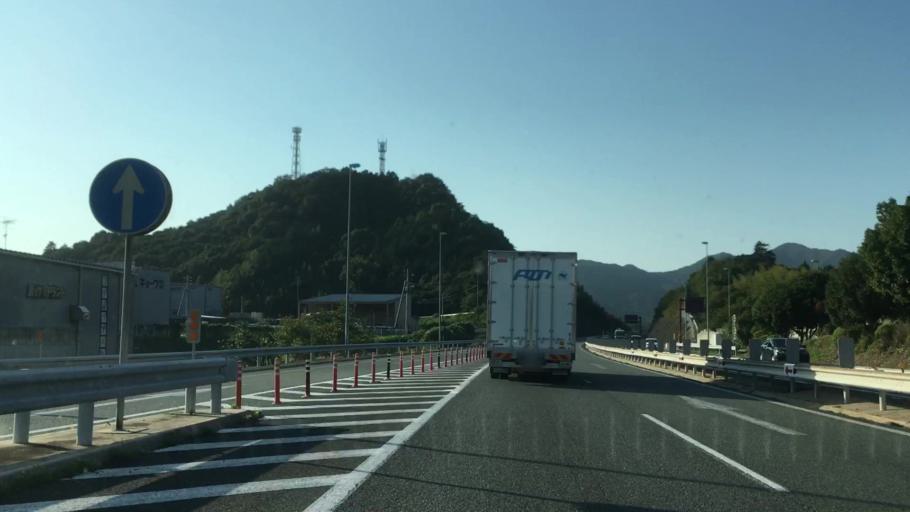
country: JP
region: Yamaguchi
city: Ogori-shimogo
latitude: 34.0884
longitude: 131.4620
